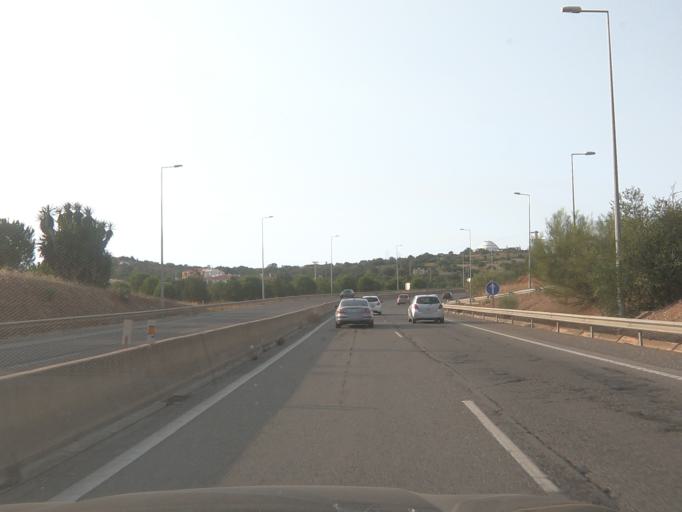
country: PT
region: Faro
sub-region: Loule
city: Loule
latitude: 37.1314
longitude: -8.0356
